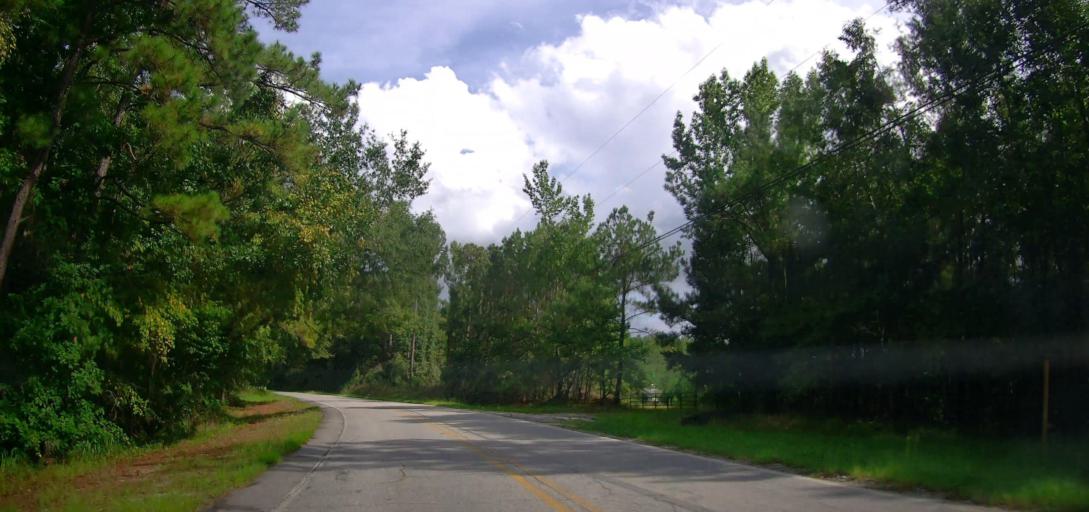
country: US
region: Alabama
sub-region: Russell County
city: Phenix City
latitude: 32.5909
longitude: -84.9363
